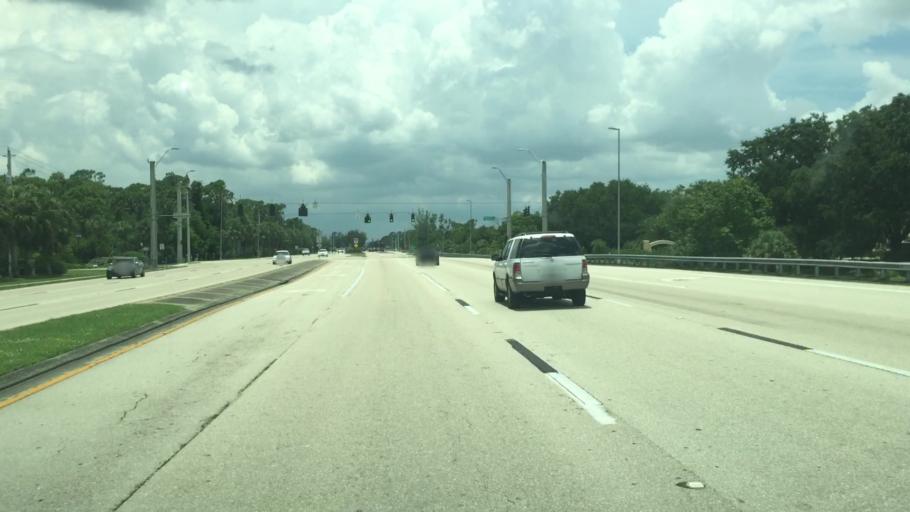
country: US
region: Florida
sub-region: Lee County
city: Villas
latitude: 26.5464
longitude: -81.8626
